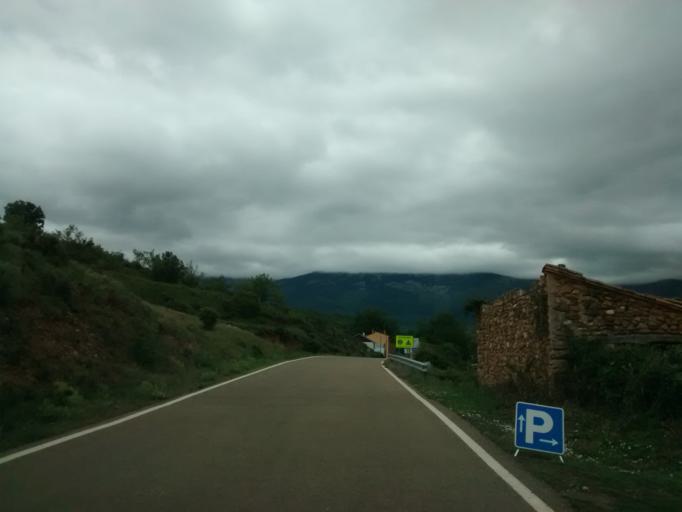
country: ES
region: Aragon
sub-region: Provincia de Zaragoza
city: Lituenigo
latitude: 41.8366
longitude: -1.7569
